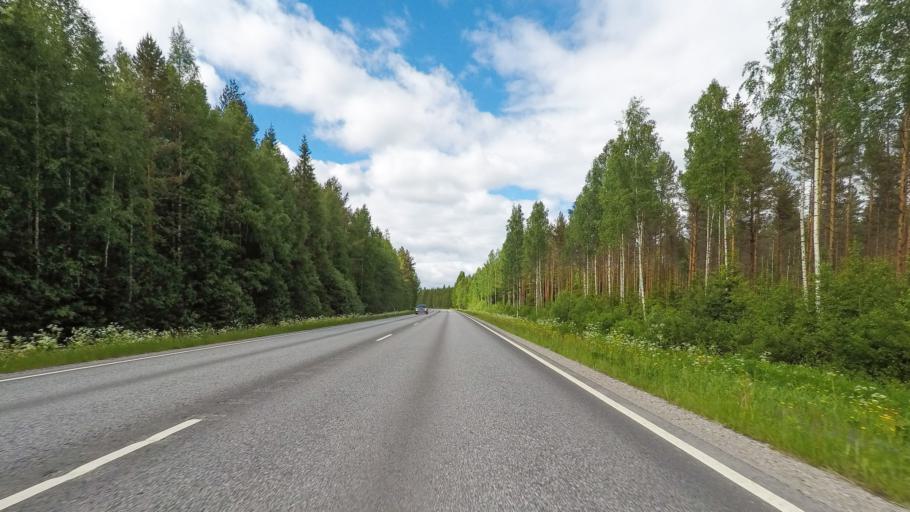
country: FI
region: Central Finland
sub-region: Jyvaeskylae
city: Toivakka
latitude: 62.2217
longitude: 26.2025
